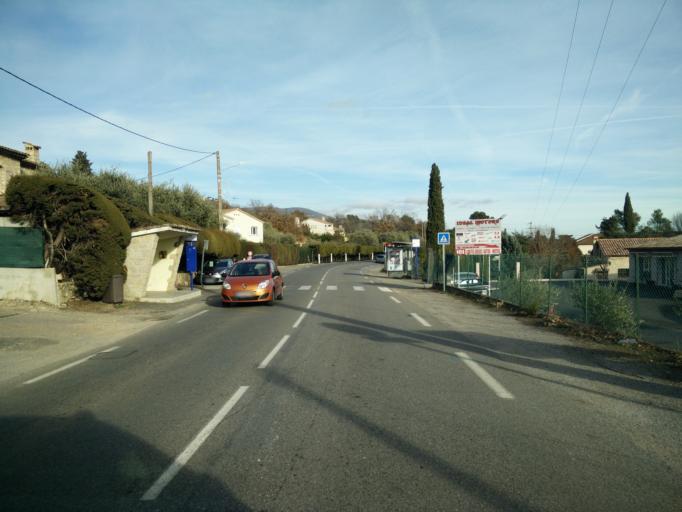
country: FR
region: Provence-Alpes-Cote d'Azur
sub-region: Departement des Alpes-Maritimes
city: Le Tignet
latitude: 43.6339
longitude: 6.8503
